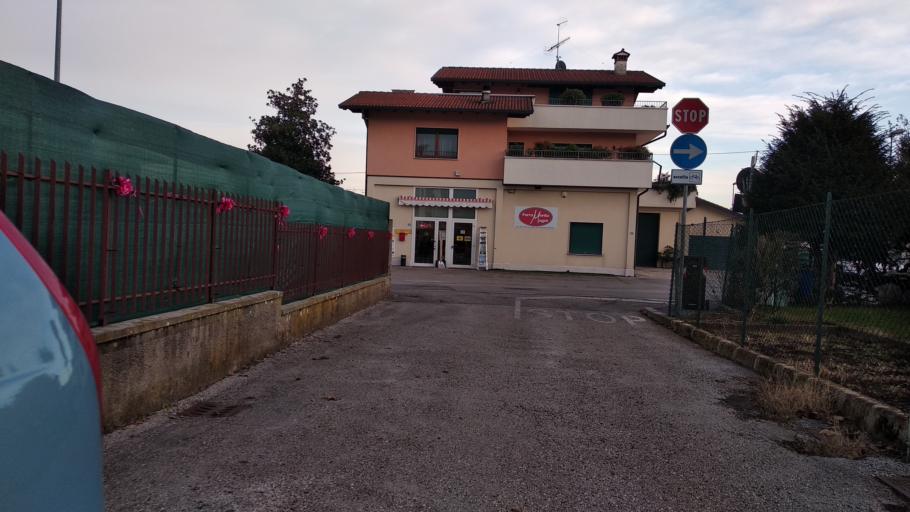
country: IT
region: Veneto
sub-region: Provincia di Vicenza
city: Schio
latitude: 45.7038
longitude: 11.3561
